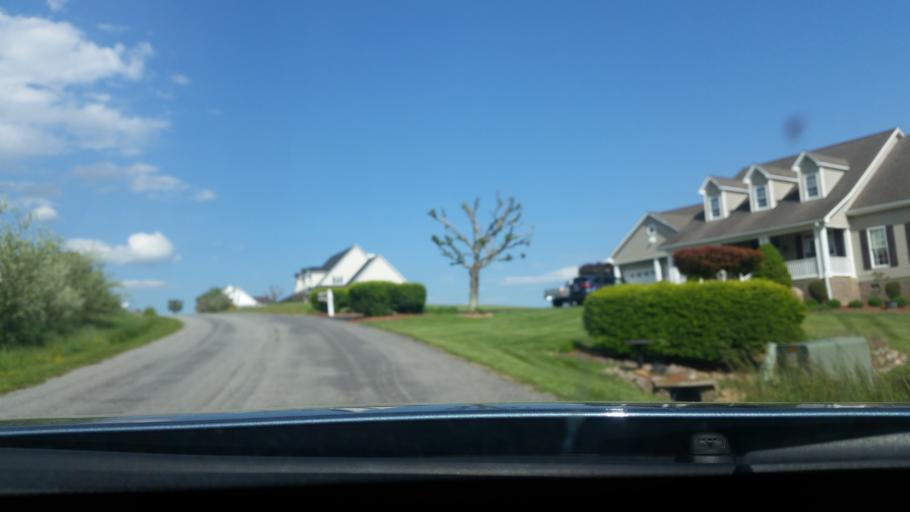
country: US
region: Virginia
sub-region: Giles County
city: Pembroke
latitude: 37.3065
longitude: -80.6355
